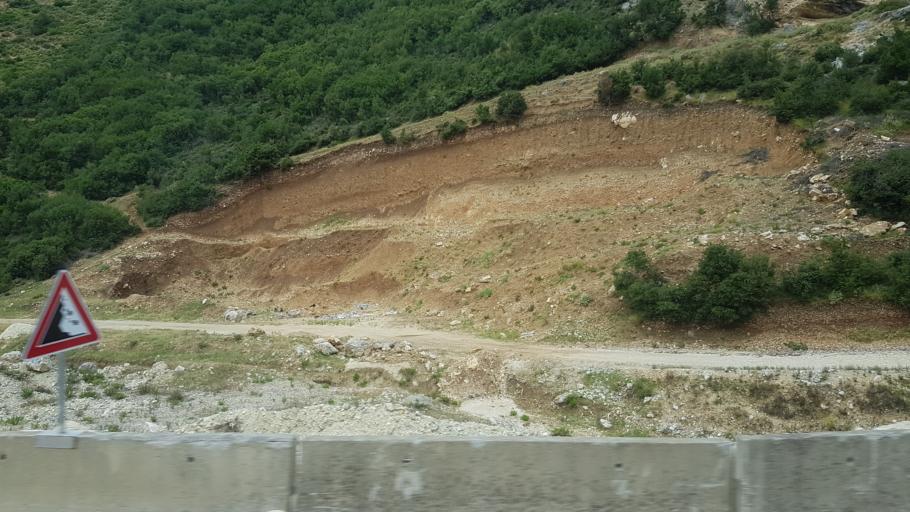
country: AL
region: Fier
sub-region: Rrethi i Mallakastres
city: Kute
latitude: 40.5104
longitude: 19.7523
